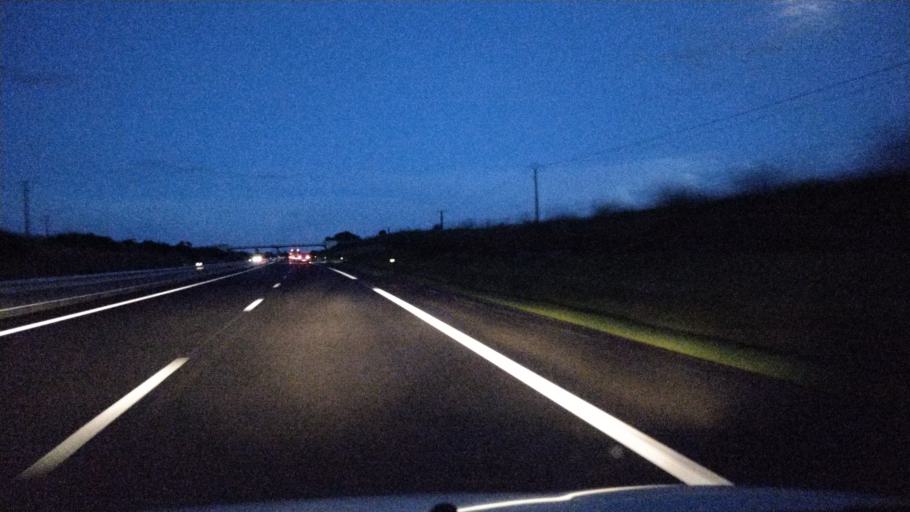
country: FR
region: Brittany
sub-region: Departement d'Ille-et-Vilaine
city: Quedillac
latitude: 48.1905
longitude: -2.1237
